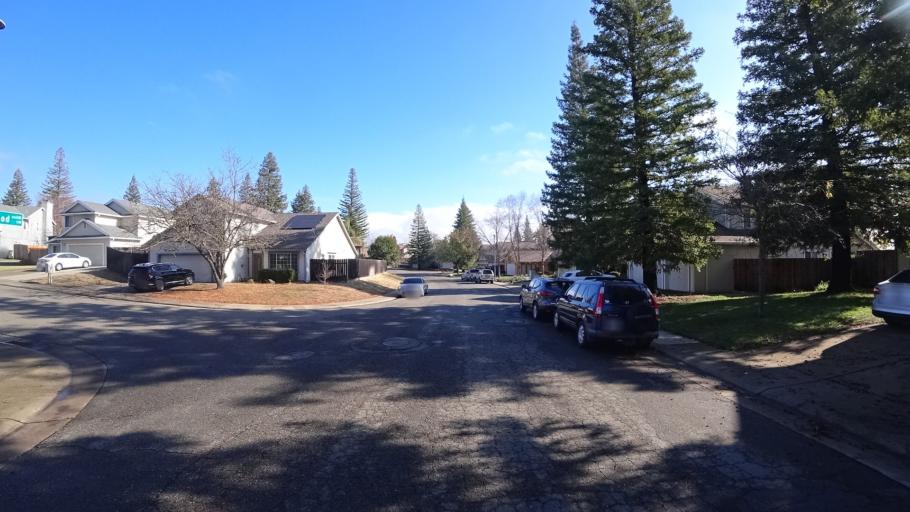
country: US
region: California
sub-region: Sacramento County
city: Antelope
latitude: 38.6871
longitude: -121.3299
